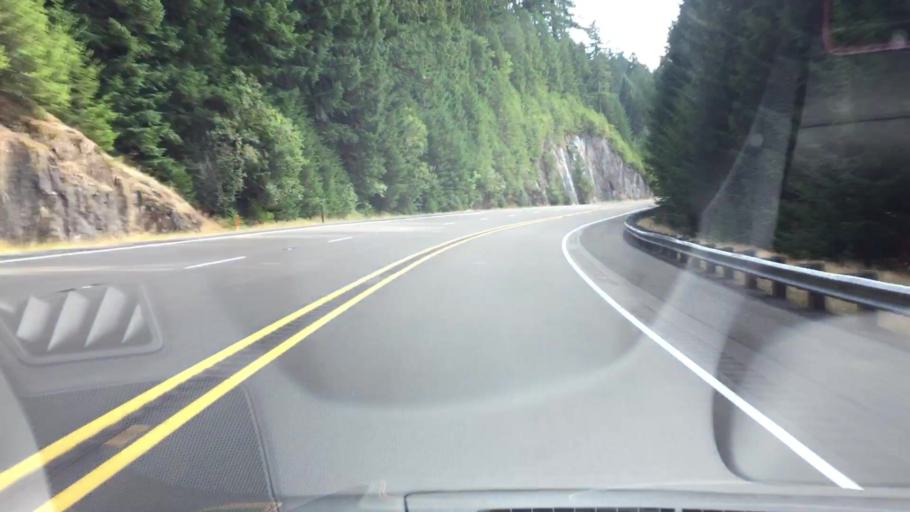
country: US
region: Washington
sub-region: Pierce County
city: Buckley
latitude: 46.6649
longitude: -121.5960
